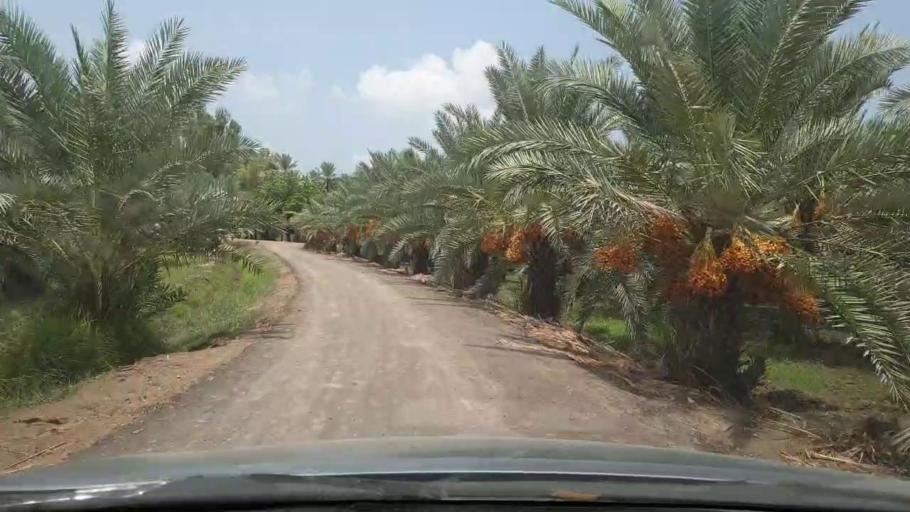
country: PK
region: Sindh
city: Khairpur
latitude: 27.4709
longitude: 68.7328
